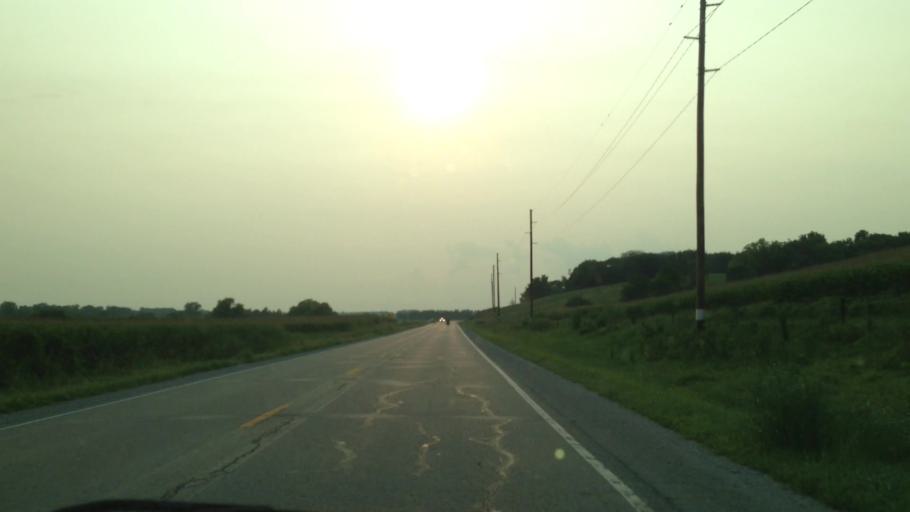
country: US
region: Iowa
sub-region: Benton County
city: Walford
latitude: 41.7979
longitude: -91.9222
